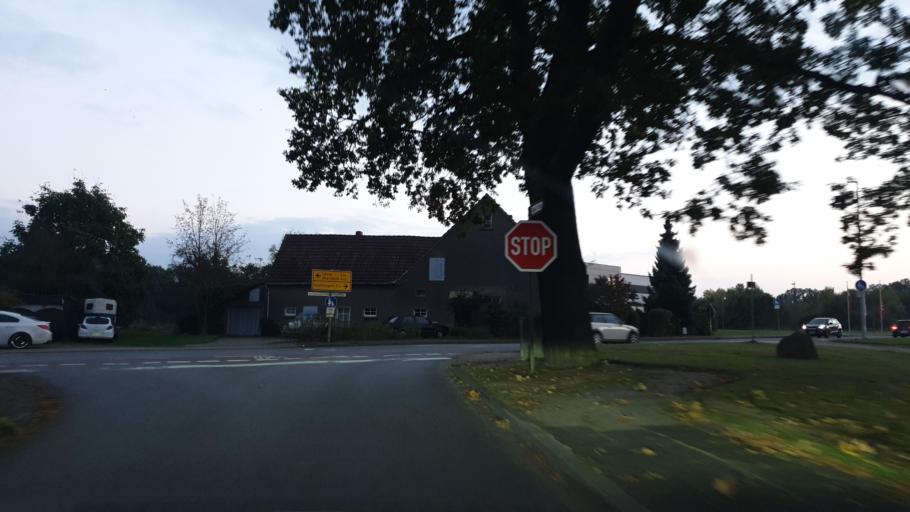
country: DE
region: North Rhine-Westphalia
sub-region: Regierungsbezirk Detmold
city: Kirchlengern
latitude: 52.2045
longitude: 8.6527
